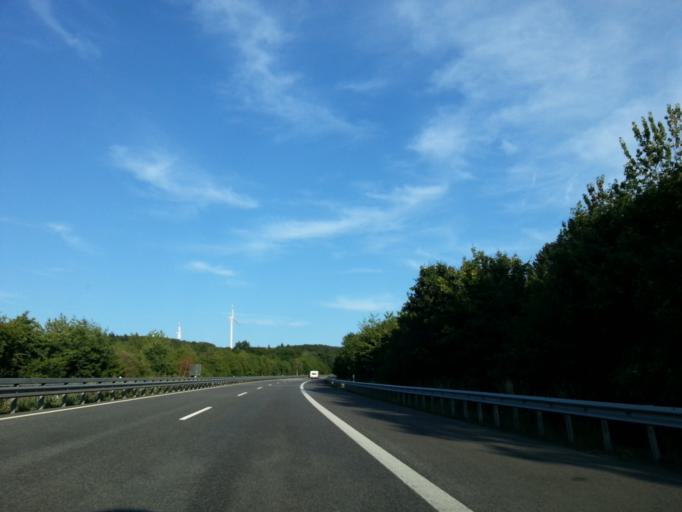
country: DE
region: Rheinland-Pfalz
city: Hoppstadten-Weiersbach
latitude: 49.6008
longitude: 7.1835
